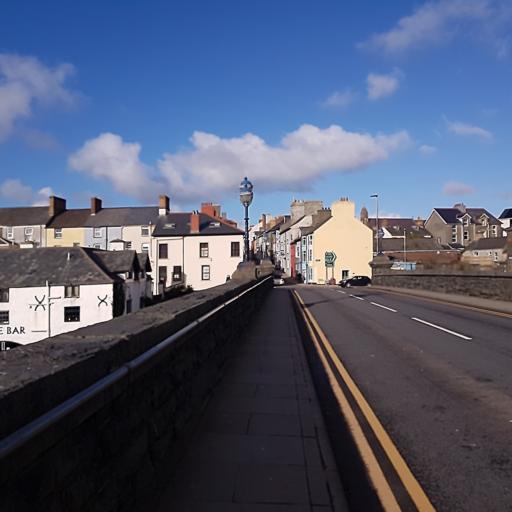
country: GB
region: Wales
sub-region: County of Ceredigion
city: Aberystwyth
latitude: 52.4115
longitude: -4.0852
